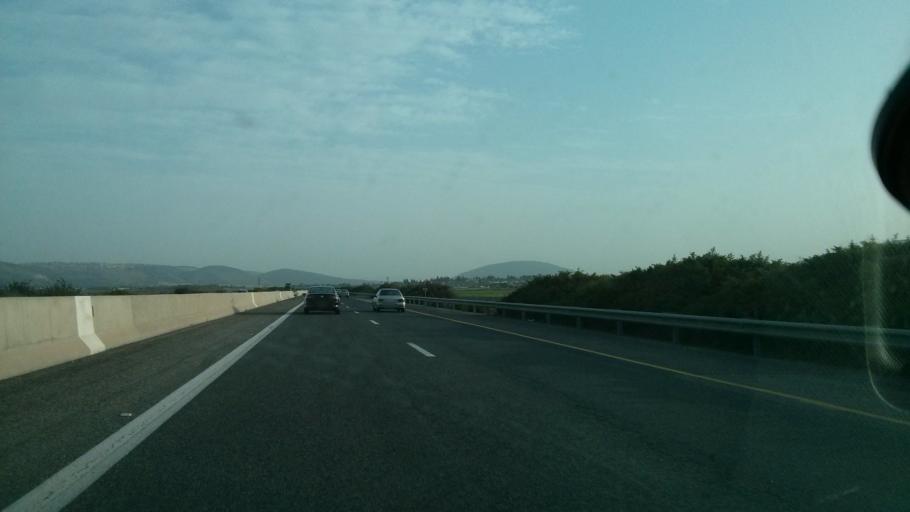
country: IL
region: Northern District
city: `Afula `Illit
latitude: 32.6112
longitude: 35.2706
